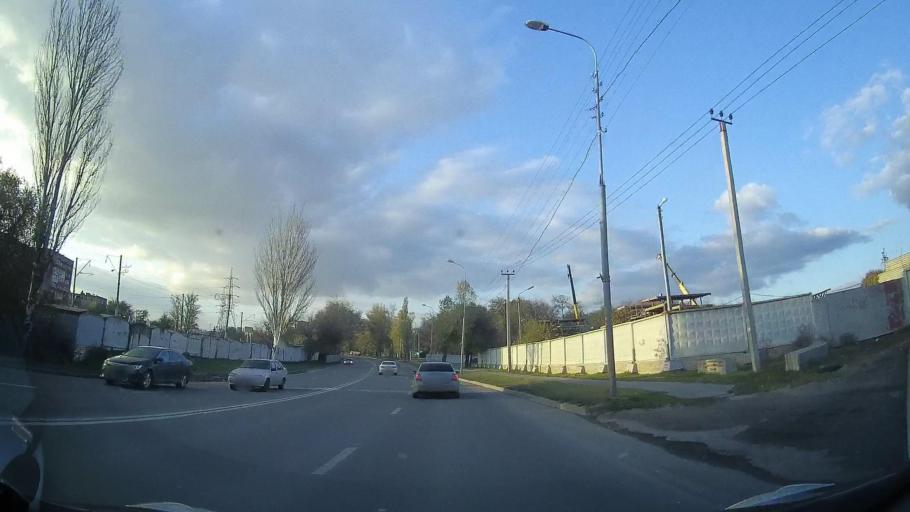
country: RU
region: Rostov
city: Imeni Chkalova
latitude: 47.2572
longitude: 39.7934
